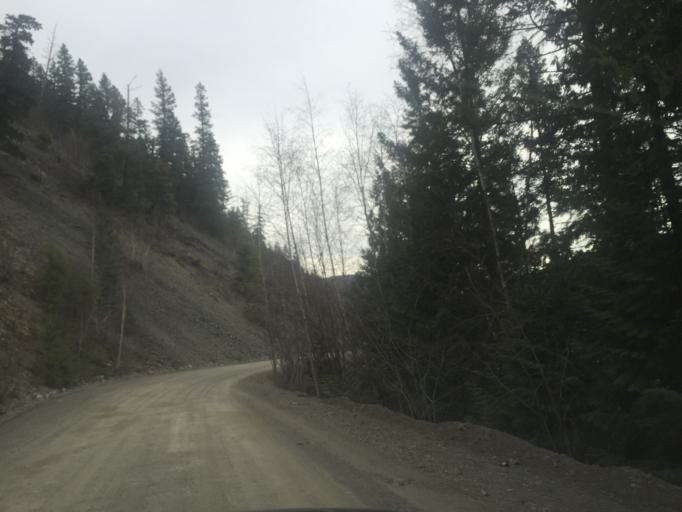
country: CA
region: British Columbia
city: Chase
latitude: 51.4247
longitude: -120.1347
